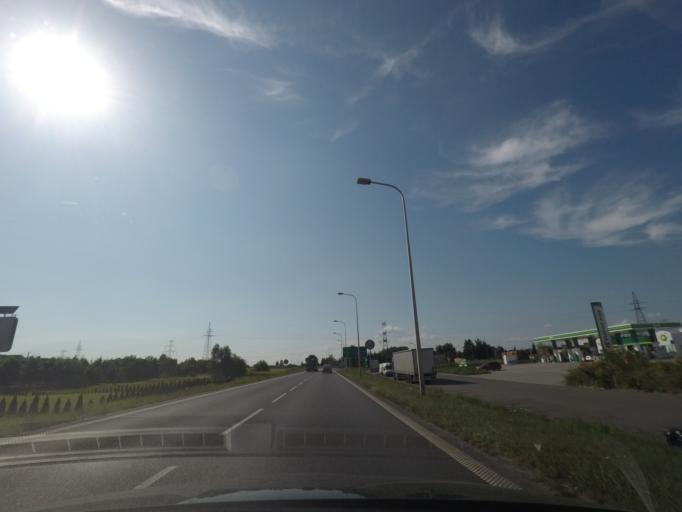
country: PL
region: Silesian Voivodeship
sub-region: Zory
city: Zory
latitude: 50.0605
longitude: 18.6680
